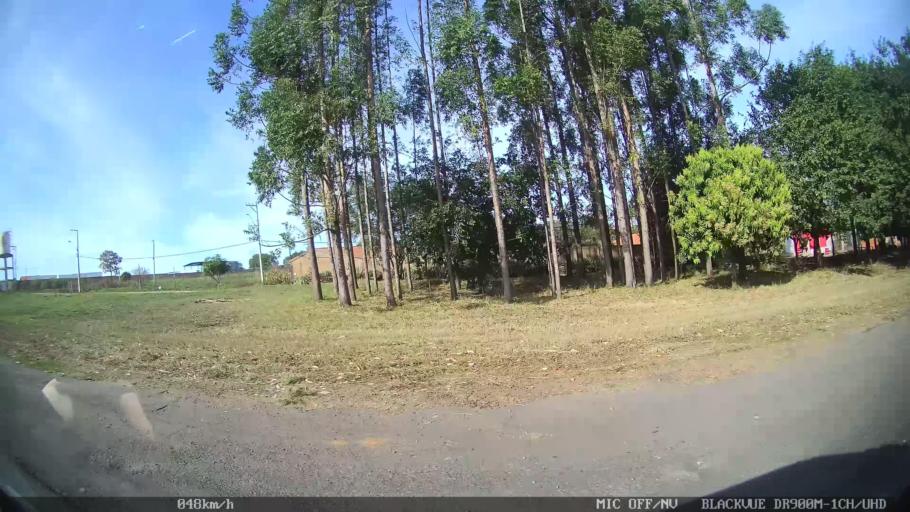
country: BR
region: Sao Paulo
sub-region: Rio Das Pedras
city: Rio das Pedras
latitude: -22.7971
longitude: -47.6051
